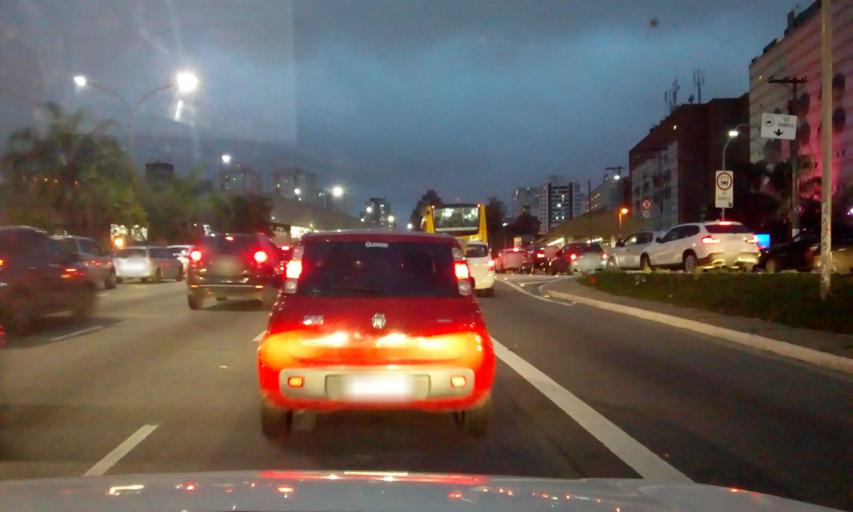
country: BR
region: Sao Paulo
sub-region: Sao Paulo
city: Sao Paulo
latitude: -23.5415
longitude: -46.5783
